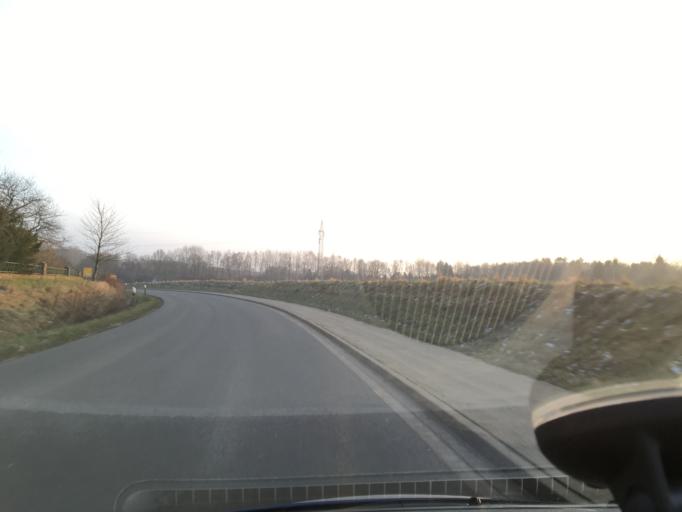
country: DE
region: Lower Saxony
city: Vastorf
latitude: 53.2044
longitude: 10.5448
